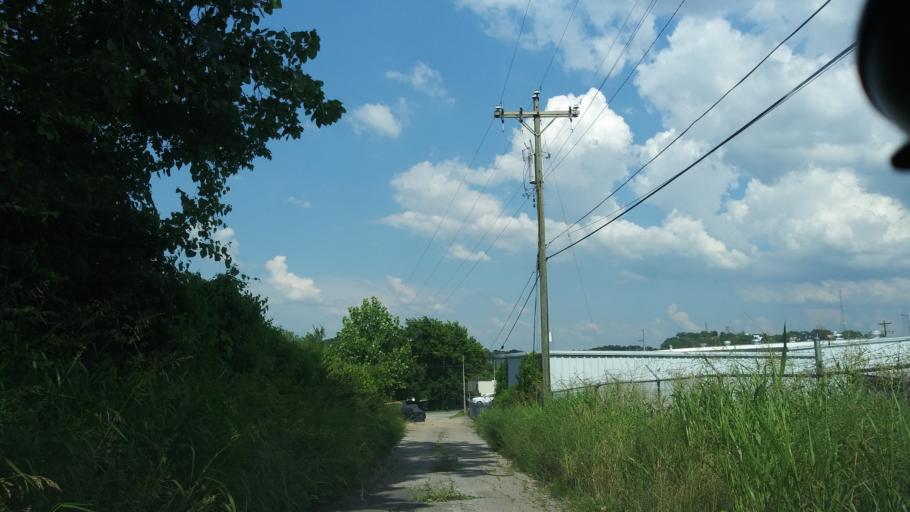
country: US
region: Tennessee
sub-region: Davidson County
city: Nashville
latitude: 36.1596
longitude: -86.8414
